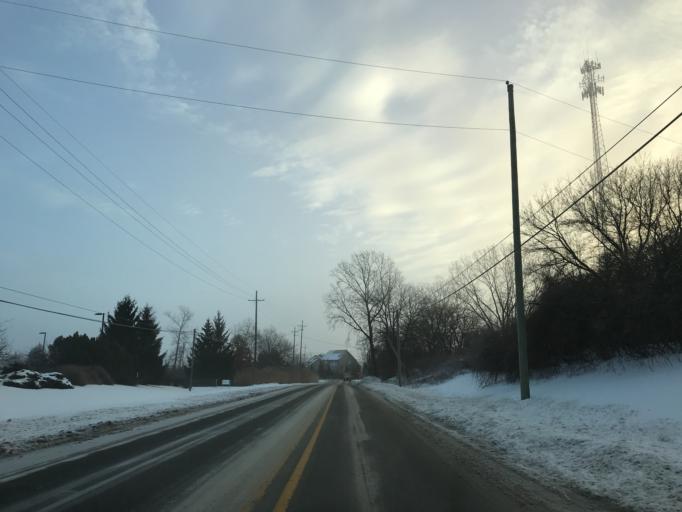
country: US
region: Michigan
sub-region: Oakland County
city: Wixom
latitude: 42.4928
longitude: -83.5581
